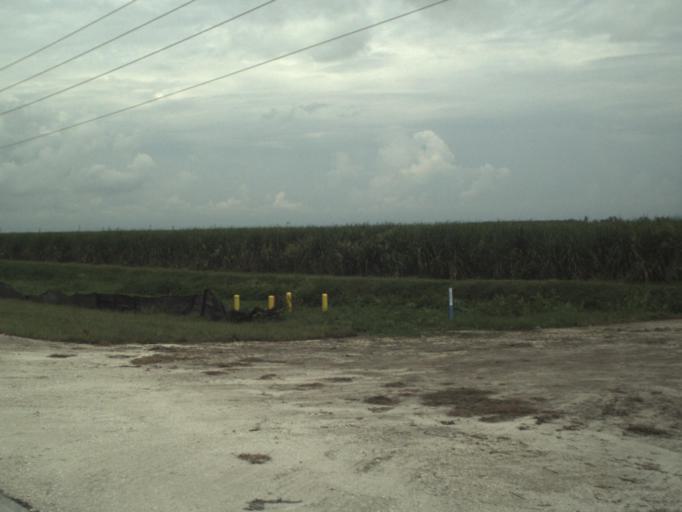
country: US
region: Florida
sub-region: Palm Beach County
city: Belle Glade
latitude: 26.7257
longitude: -80.6761
